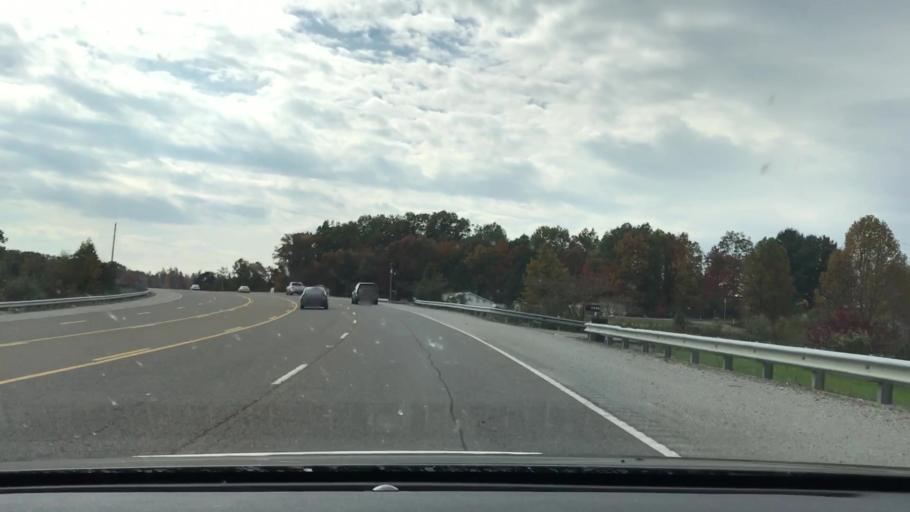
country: US
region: Tennessee
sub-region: Scott County
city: Oneida
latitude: 36.4806
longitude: -84.5386
